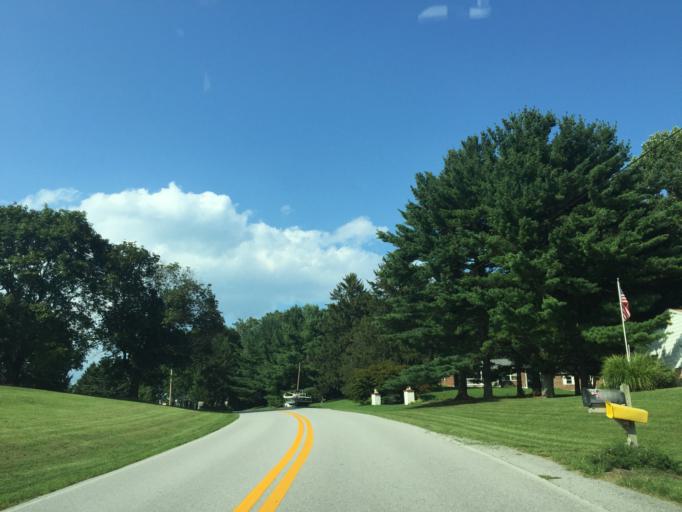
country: US
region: Maryland
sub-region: Carroll County
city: Manchester
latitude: 39.6335
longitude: -76.8851
